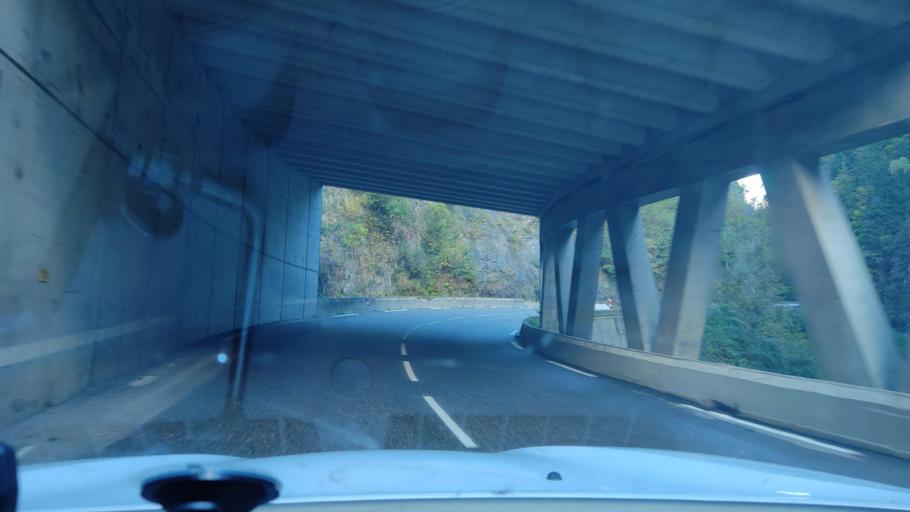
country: FR
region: Rhone-Alpes
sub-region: Departement de la Savoie
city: Ugine
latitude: 45.7819
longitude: 6.4848
